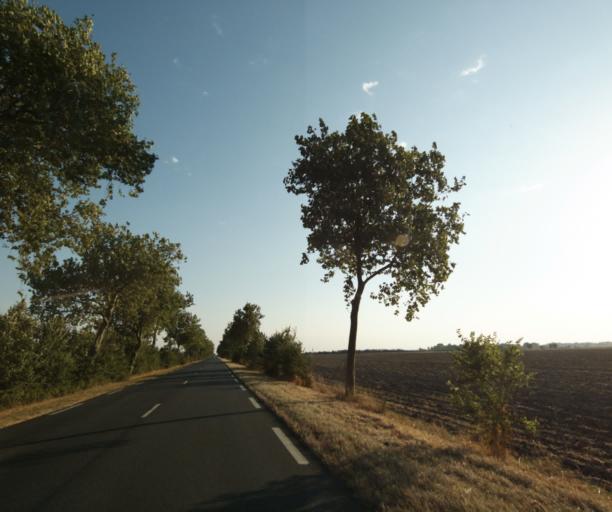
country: FR
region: Poitou-Charentes
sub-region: Departement de la Charente-Maritime
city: Tonnay-Charente
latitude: 45.9683
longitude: -0.9214
